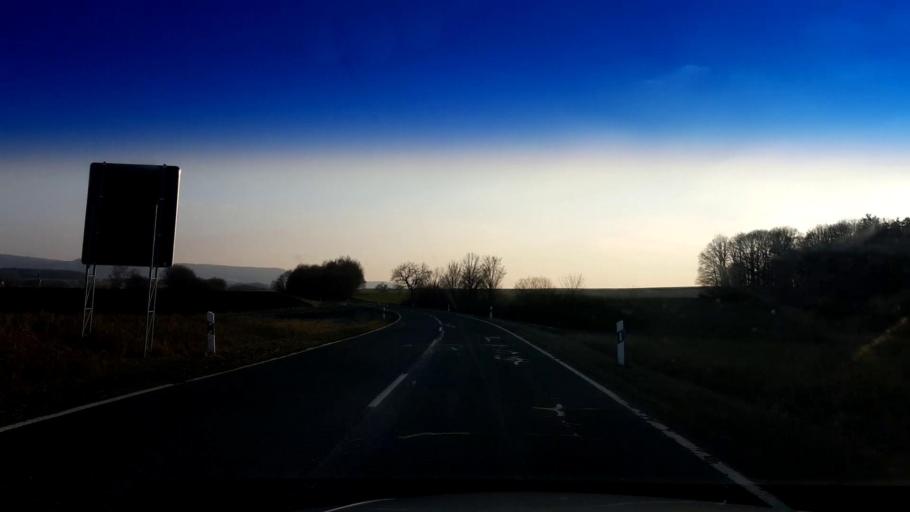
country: DE
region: Bavaria
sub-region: Upper Franconia
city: Schesslitz
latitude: 50.0134
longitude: 11.0109
